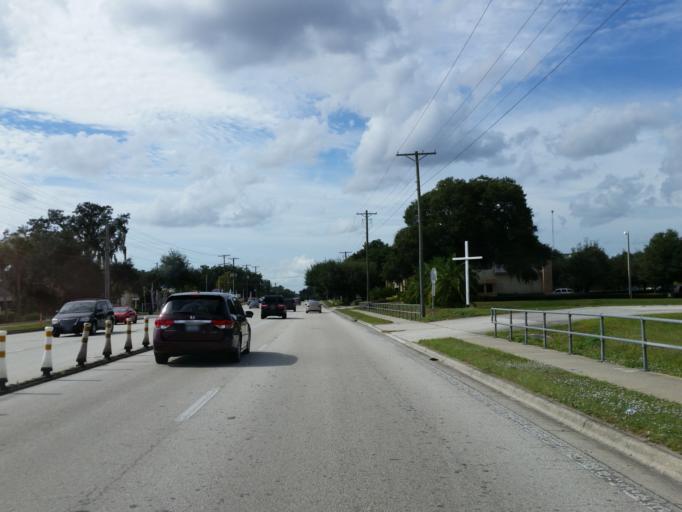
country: US
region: Florida
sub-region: Hillsborough County
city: Bloomingdale
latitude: 27.8938
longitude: -82.2724
